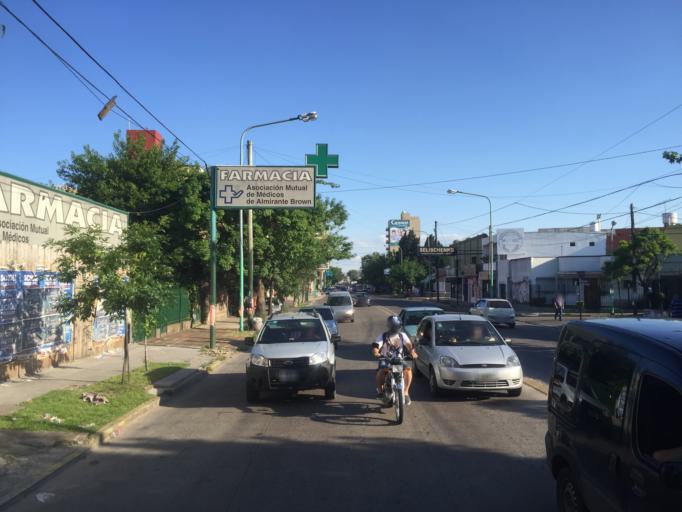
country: AR
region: Buenos Aires
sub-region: Partido de Lomas de Zamora
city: Lomas de Zamora
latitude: -34.7727
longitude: -58.3947
